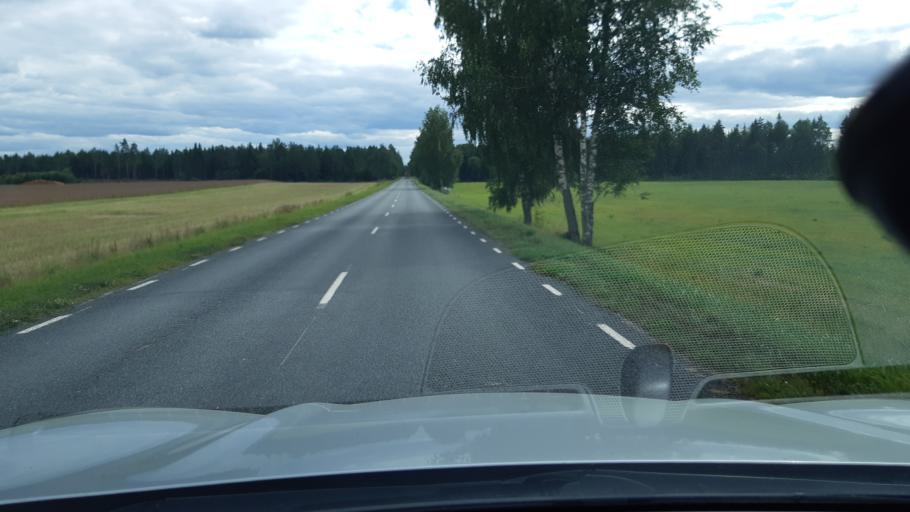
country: EE
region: Raplamaa
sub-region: Maerjamaa vald
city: Marjamaa
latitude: 59.0369
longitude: 24.5512
